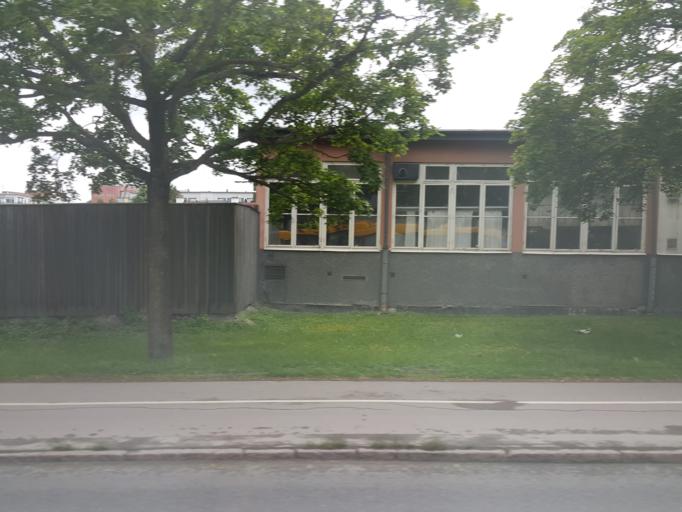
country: SE
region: Uppsala
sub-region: Uppsala Kommun
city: Uppsala
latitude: 59.8530
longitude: 17.6538
